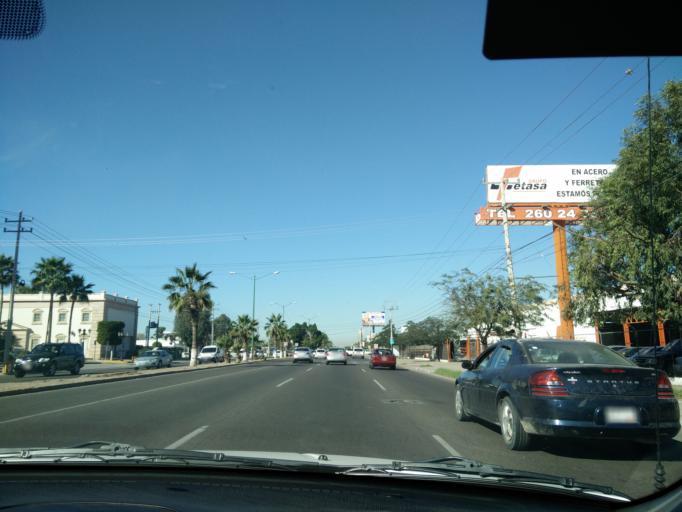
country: MX
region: Sonora
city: Hermosillo
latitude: 29.0944
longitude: -110.9986
